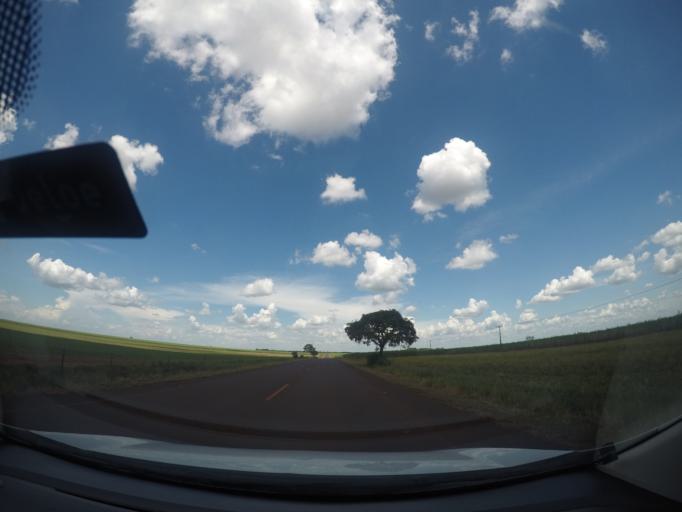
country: BR
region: Minas Gerais
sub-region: Frutal
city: Frutal
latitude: -19.9225
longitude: -48.6747
